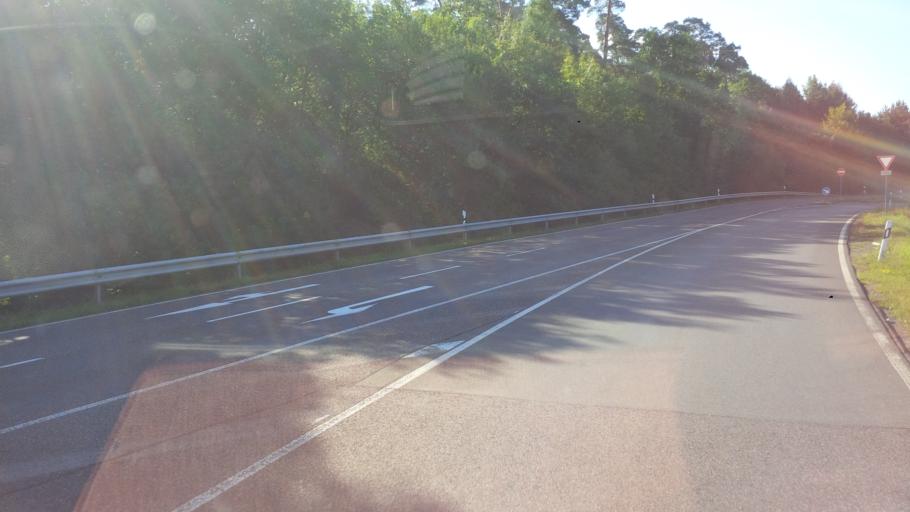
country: DE
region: Hesse
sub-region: Regierungsbezirk Darmstadt
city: Wehrheim
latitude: 50.2834
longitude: 8.5696
